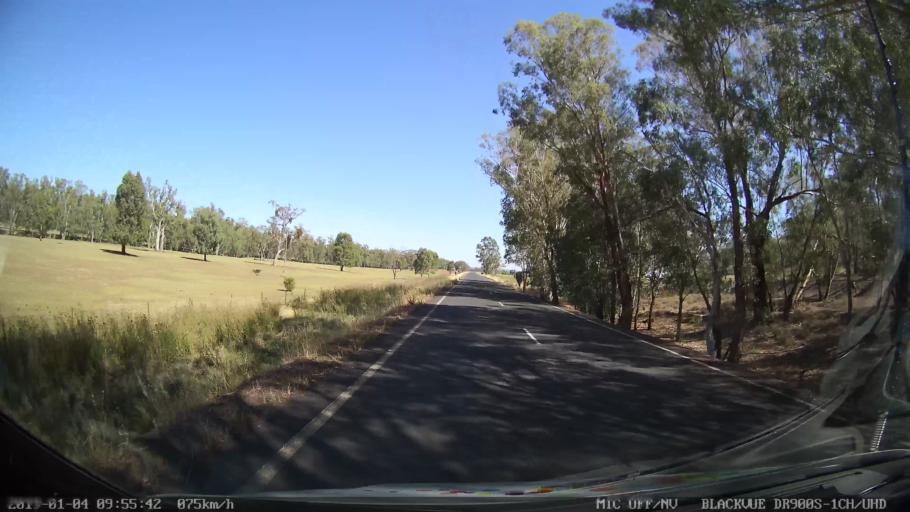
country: AU
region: New South Wales
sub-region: Cabonne
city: Canowindra
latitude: -33.5323
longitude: 148.4024
